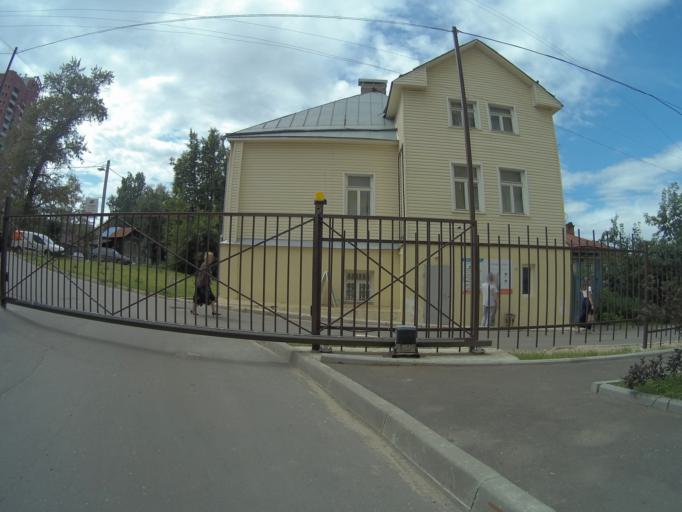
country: RU
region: Vladimir
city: Vladimir
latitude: 56.1242
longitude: 40.3834
